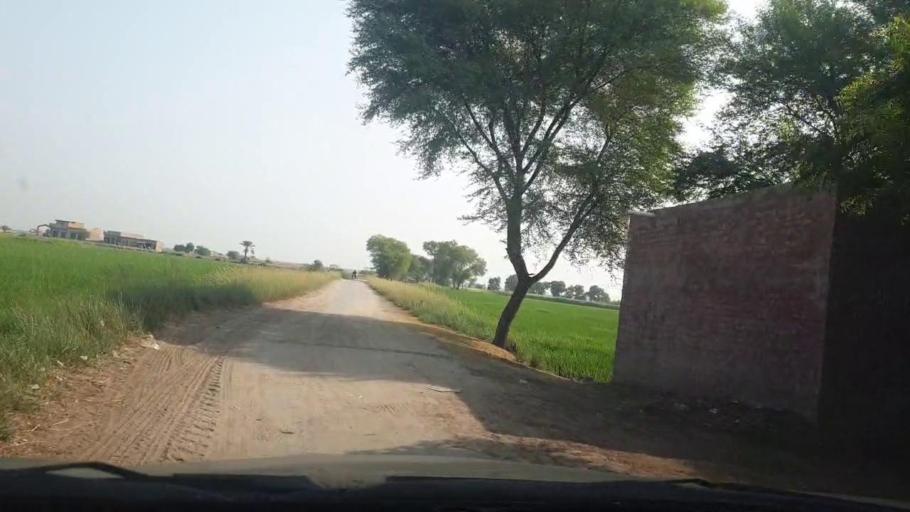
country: PK
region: Sindh
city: Larkana
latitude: 27.5876
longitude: 68.1879
